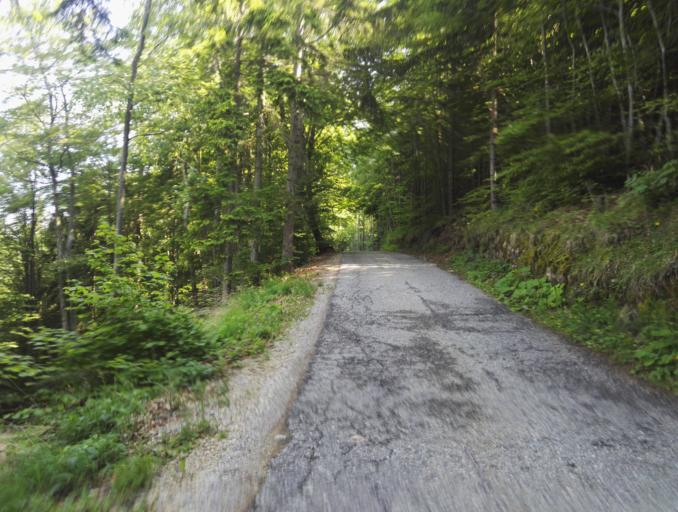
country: AT
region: Styria
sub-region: Politischer Bezirk Graz-Umgebung
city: Semriach
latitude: 47.1844
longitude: 15.4236
